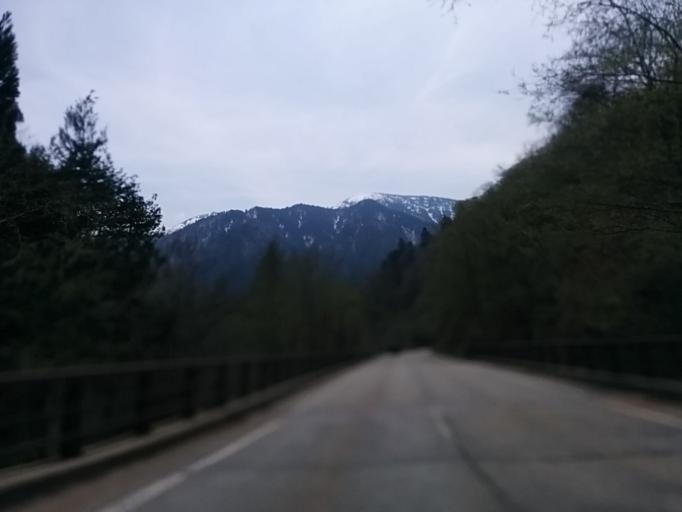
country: JP
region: Gifu
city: Takayama
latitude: 36.1923
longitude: 137.5478
